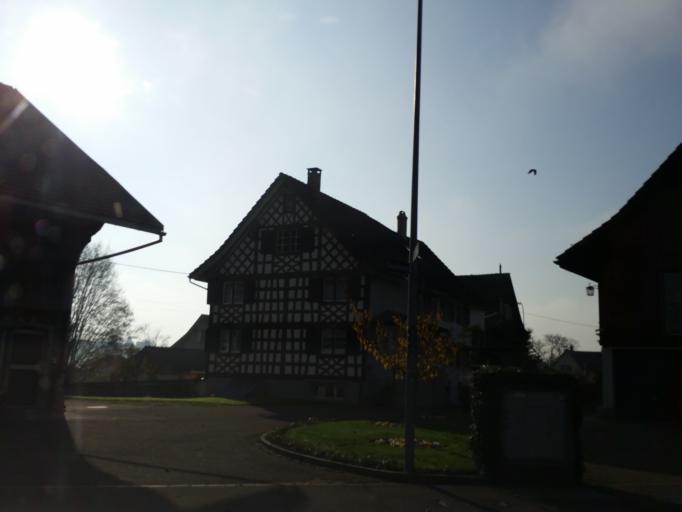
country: CH
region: Thurgau
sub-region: Arbon District
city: Arbon
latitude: 47.5277
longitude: 9.4067
